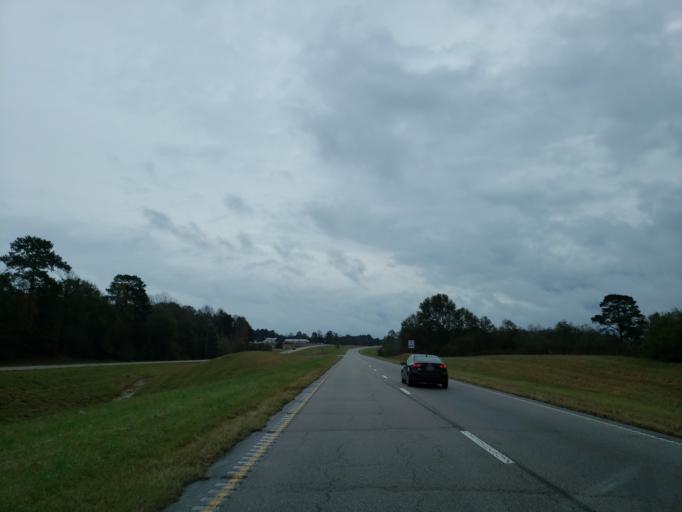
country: US
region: Mississippi
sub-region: Jones County
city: Sharon
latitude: 31.7036
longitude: -88.9163
